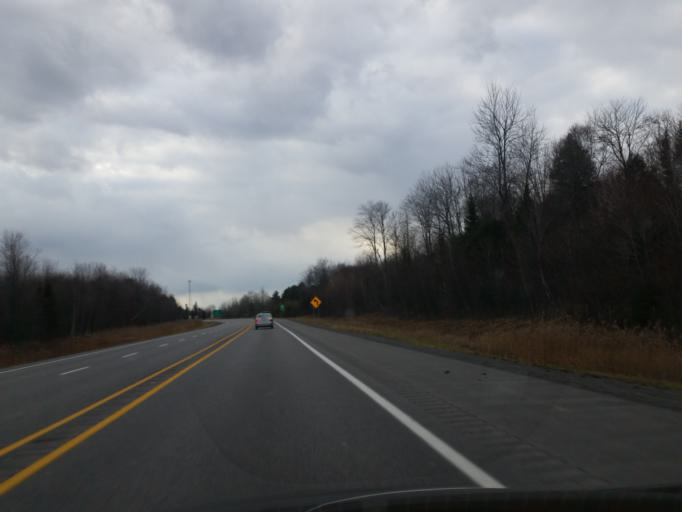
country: CA
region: Quebec
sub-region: Laurentides
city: Saint-Colomban
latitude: 45.6795
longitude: -74.1668
